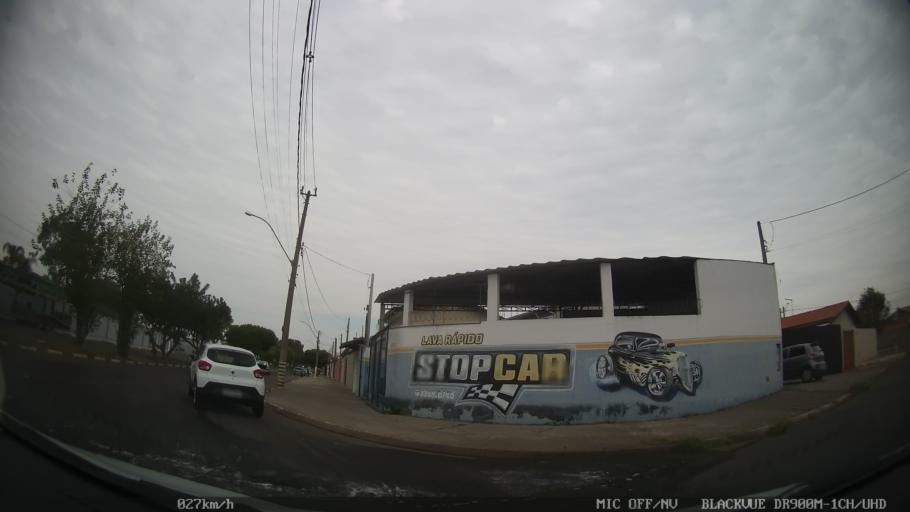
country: BR
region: Sao Paulo
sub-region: Paulinia
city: Paulinia
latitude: -22.7206
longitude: -47.1684
